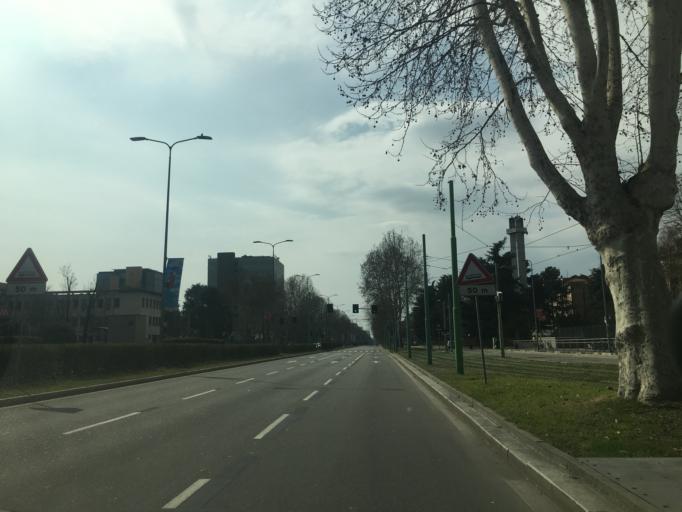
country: IT
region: Lombardy
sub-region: Citta metropolitana di Milano
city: Sesto San Giovanni
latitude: 45.5274
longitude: 9.2124
